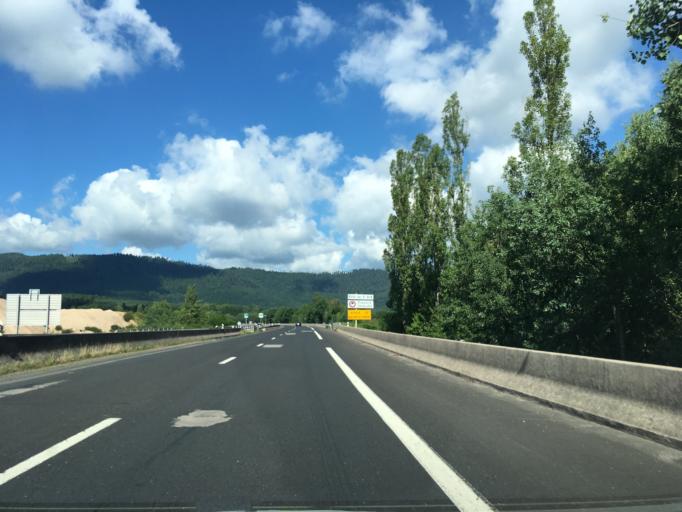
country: FR
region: Lorraine
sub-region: Departement des Vosges
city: Sainte-Marguerite
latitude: 48.2614
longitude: 6.9726
